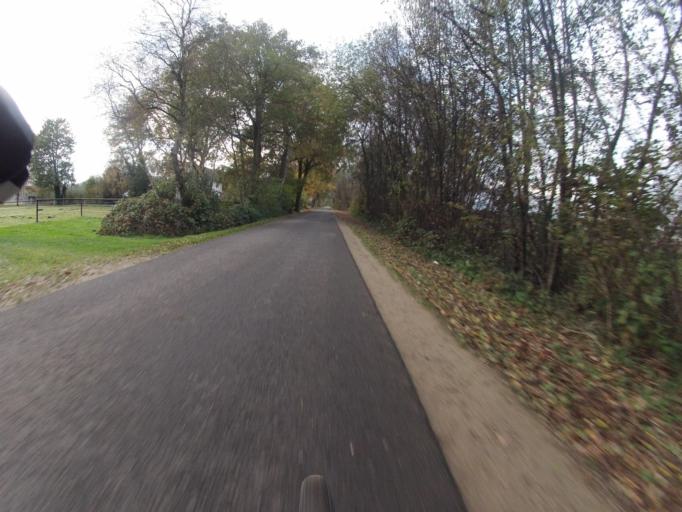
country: DE
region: North Rhine-Westphalia
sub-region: Regierungsbezirk Munster
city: Horstel
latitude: 52.2614
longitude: 7.5668
